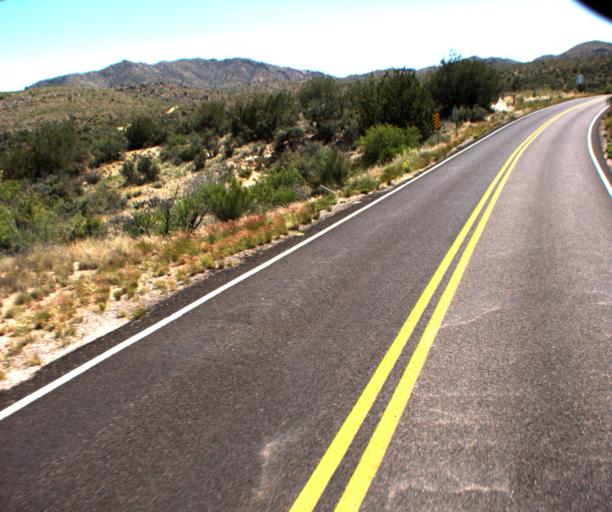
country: US
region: Arizona
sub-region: Yavapai County
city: Bagdad
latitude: 34.5205
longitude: -113.1344
